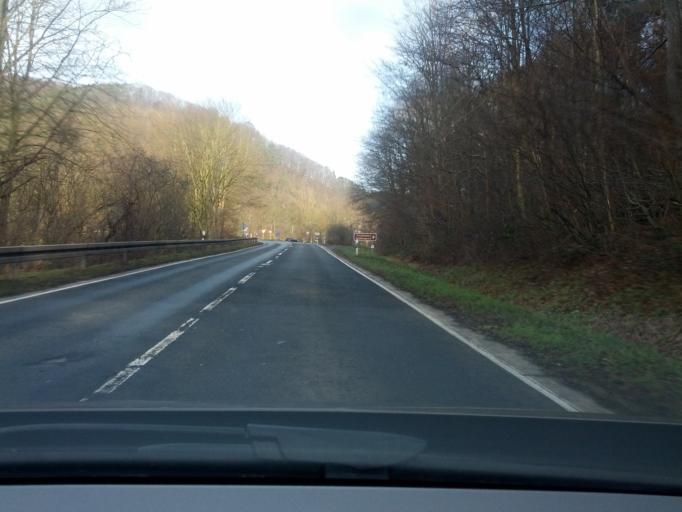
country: DE
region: Thuringia
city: Lindewerra
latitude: 51.3222
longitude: 9.9055
